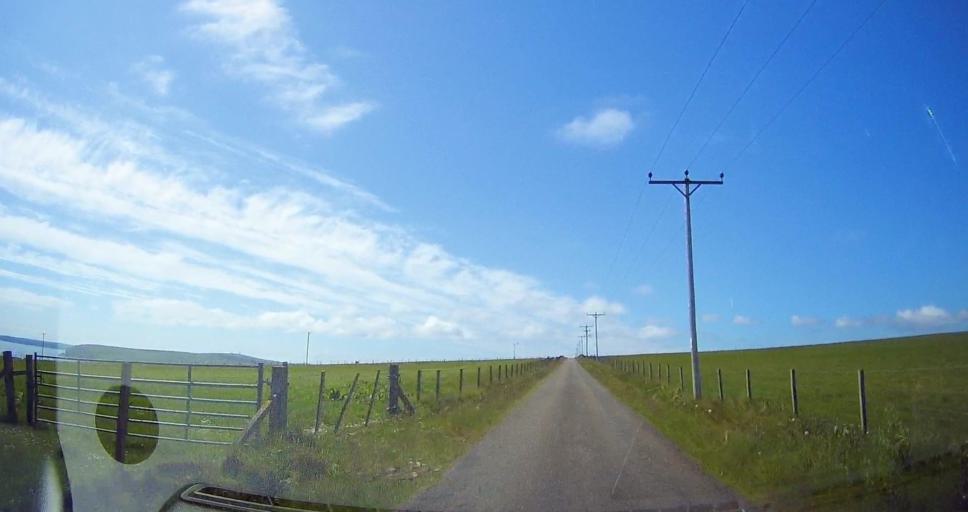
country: GB
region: Scotland
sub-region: Orkney Islands
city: Kirkwall
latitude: 58.8167
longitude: -2.9134
